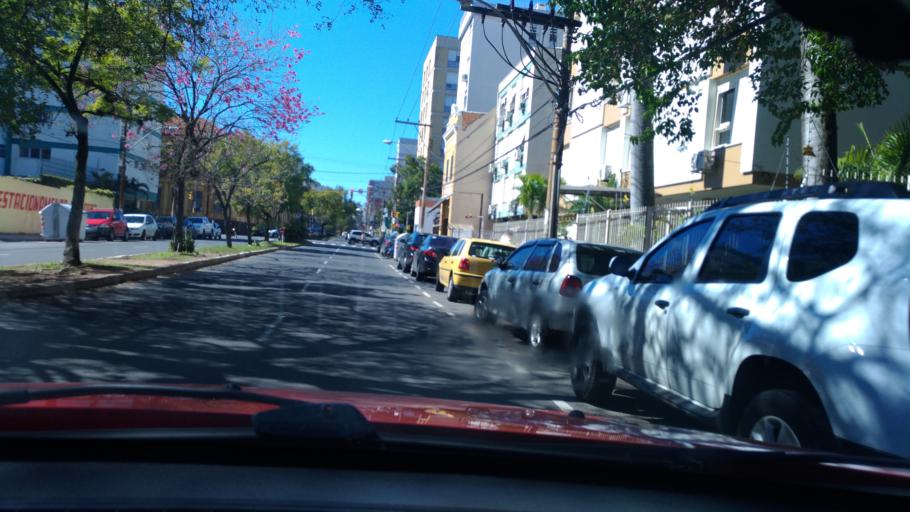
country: BR
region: Rio Grande do Sul
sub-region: Porto Alegre
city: Porto Alegre
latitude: -30.0401
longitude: -51.2145
